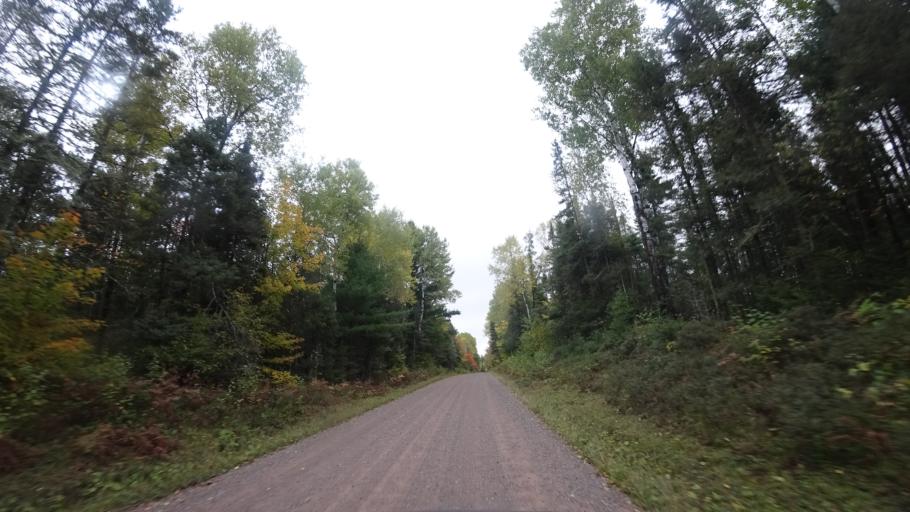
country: US
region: Wisconsin
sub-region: Sawyer County
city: Little Round Lake
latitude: 46.0704
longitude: -90.9941
